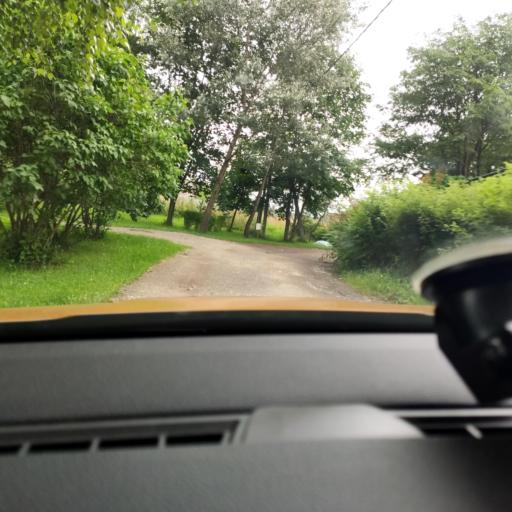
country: RU
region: Moskovskaya
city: Melikhovo
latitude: 55.1362
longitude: 37.5661
